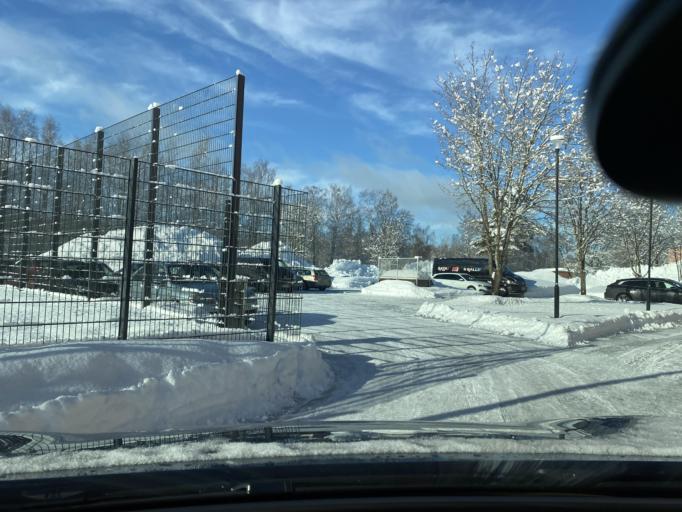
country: FI
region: Southern Savonia
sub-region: Mikkeli
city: Kangasniemi
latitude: 61.9880
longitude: 26.6358
